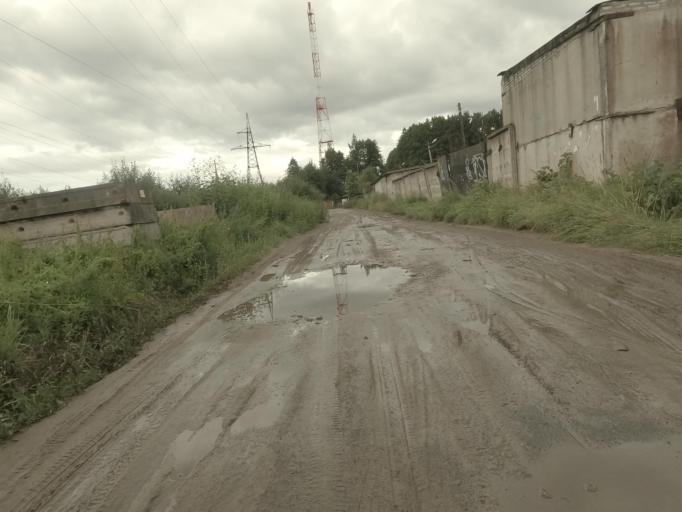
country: RU
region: Leningrad
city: Kirovsk
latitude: 59.8923
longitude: 31.0028
